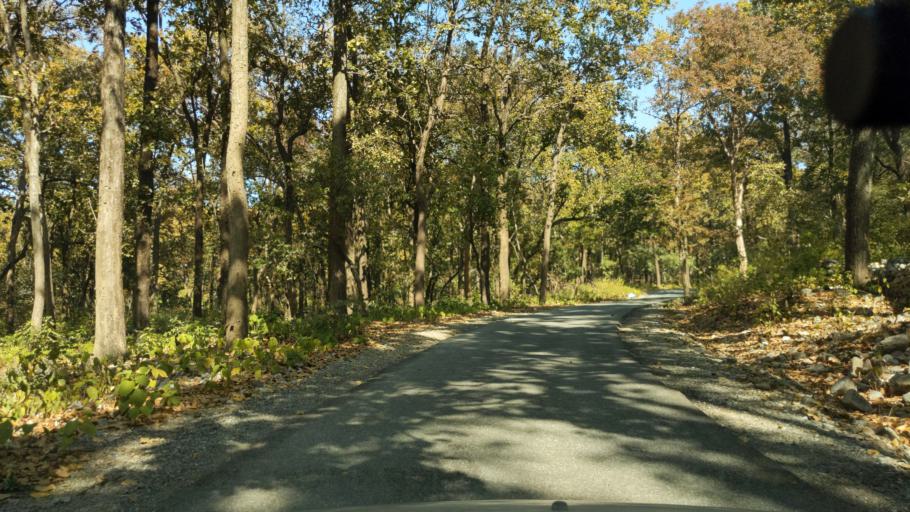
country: IN
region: Uttarakhand
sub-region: Naini Tal
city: Ramnagar
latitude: 29.4623
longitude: 79.2318
